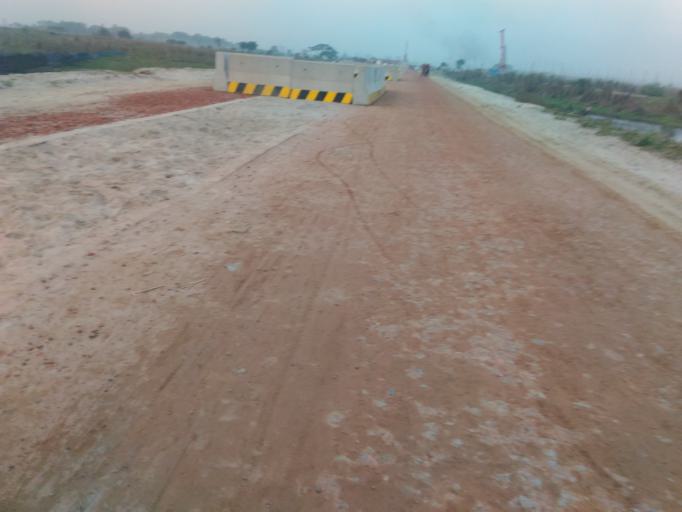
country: BD
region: Dhaka
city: Tungi
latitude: 23.8506
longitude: 90.3638
